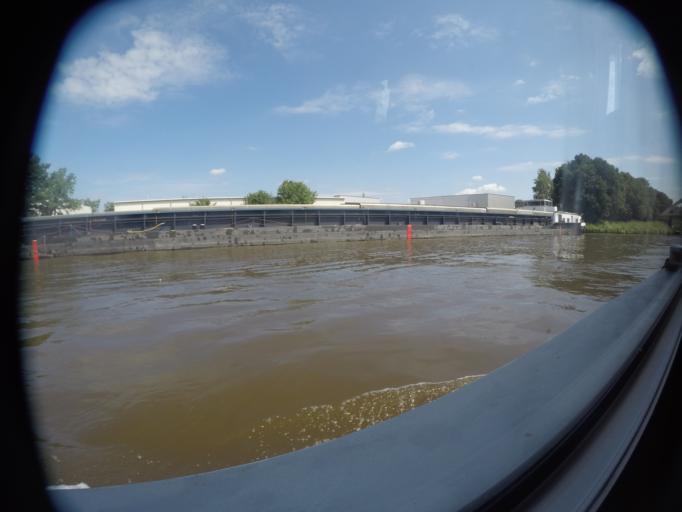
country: NL
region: Overijssel
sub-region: Gemeente Hof van Twente
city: Delden
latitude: 52.2522
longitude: 6.6966
